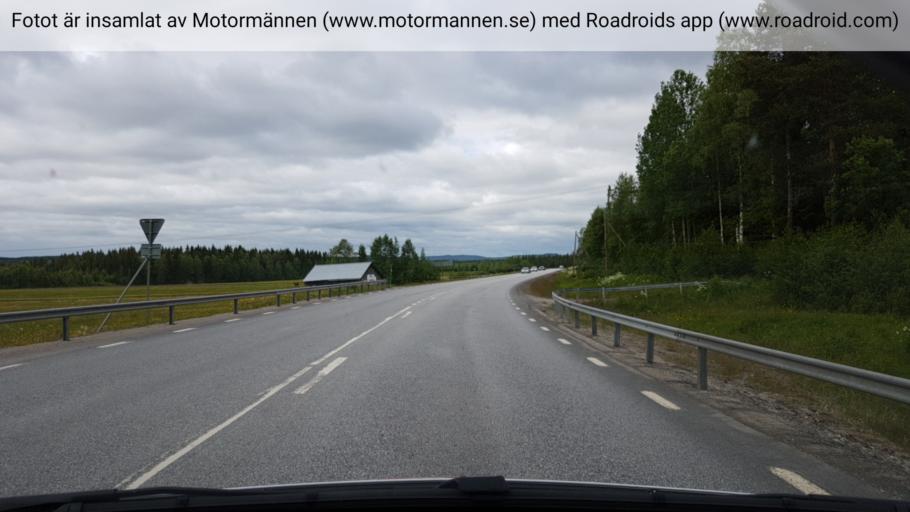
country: SE
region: Vaesterbotten
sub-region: Vannas Kommun
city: Vaennaes
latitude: 63.9239
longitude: 19.7802
